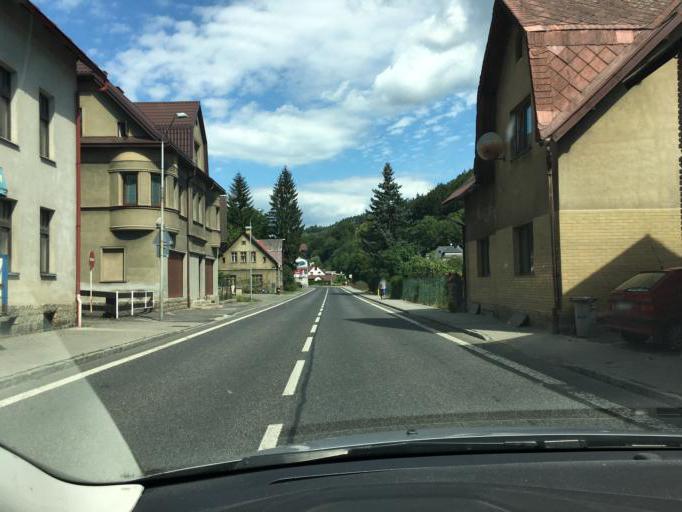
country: CZ
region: Liberecky
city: Velke Hamry
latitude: 50.7210
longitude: 15.3155
